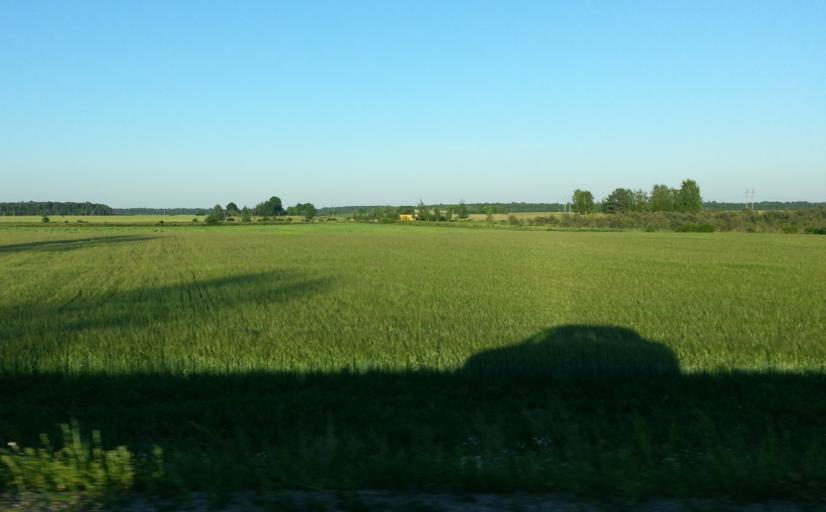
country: LT
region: Panevezys
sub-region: Panevezys City
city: Panevezys
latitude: 55.6372
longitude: 24.3487
